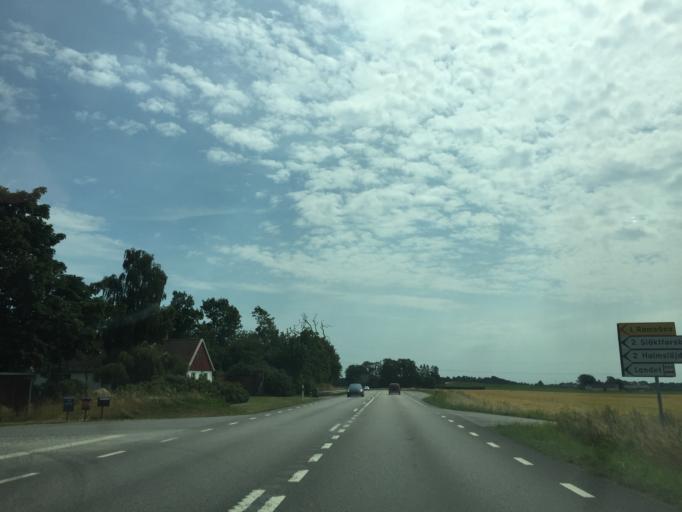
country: SE
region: Skane
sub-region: Tomelilla Kommun
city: Tomelilla
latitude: 55.5696
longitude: 13.8749
